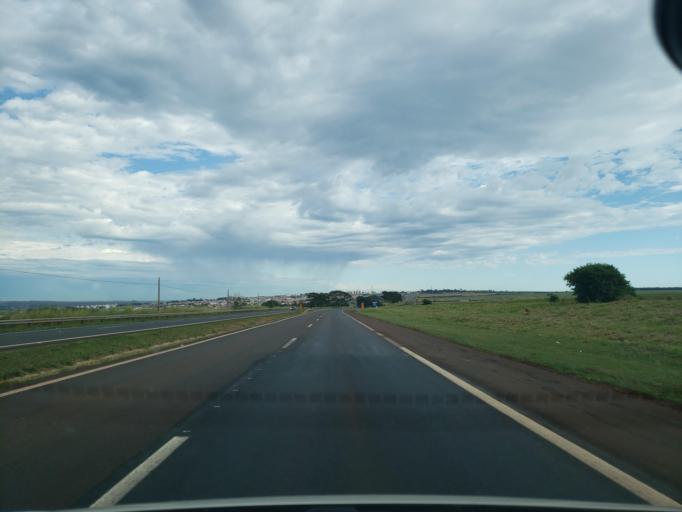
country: BR
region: Sao Paulo
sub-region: Jau
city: Jau
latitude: -22.2645
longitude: -48.5229
